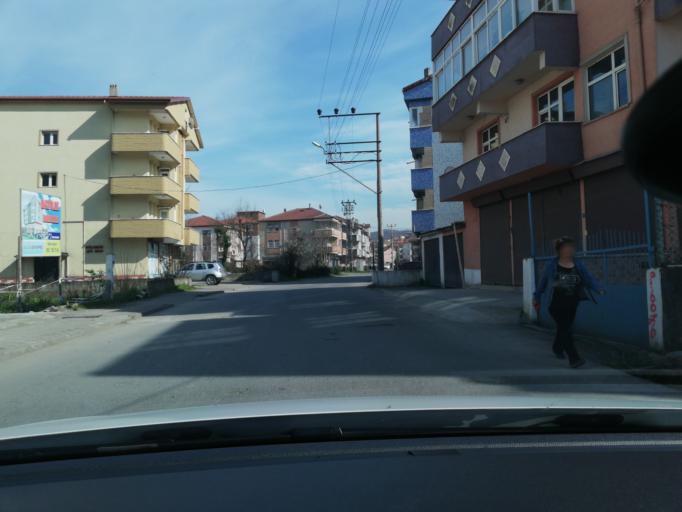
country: TR
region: Zonguldak
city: Eregli
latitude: 41.2682
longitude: 31.4491
